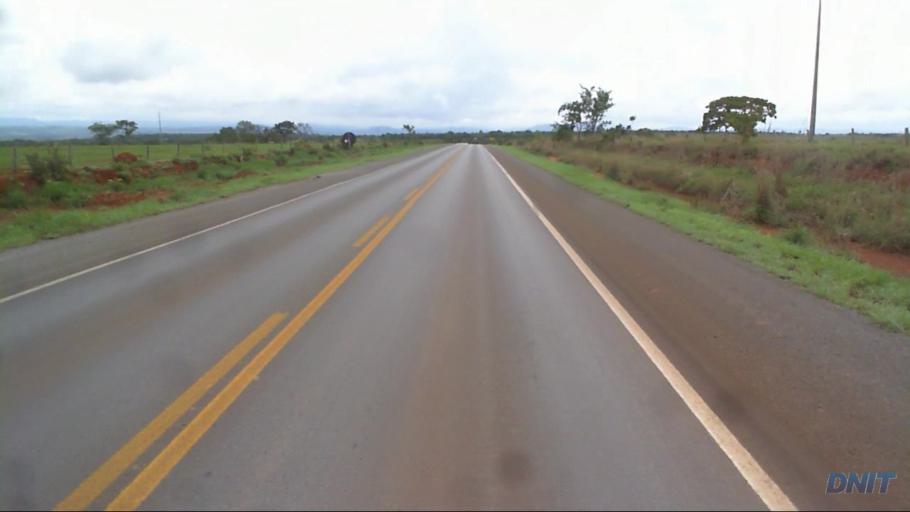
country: BR
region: Goias
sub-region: Padre Bernardo
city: Padre Bernardo
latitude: -15.1594
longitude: -48.3581
